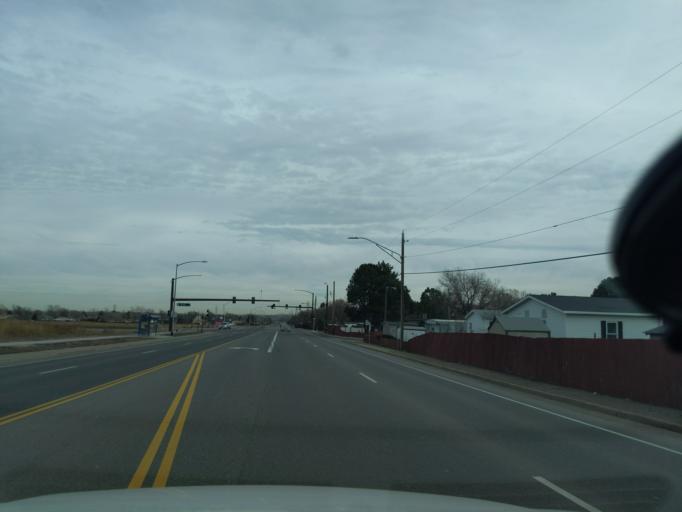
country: US
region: Colorado
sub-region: Adams County
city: Welby
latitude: 39.8560
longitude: -104.9511
